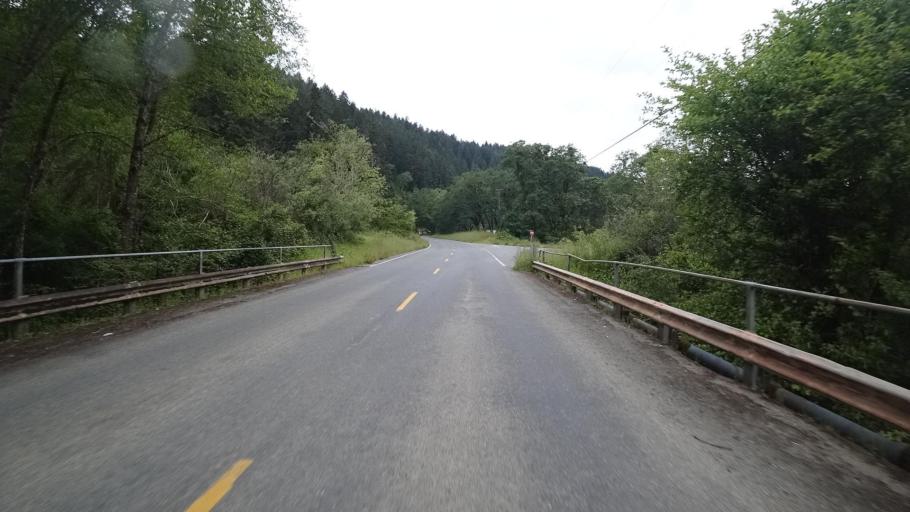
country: US
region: California
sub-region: Humboldt County
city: Willow Creek
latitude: 41.0867
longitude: -123.7087
